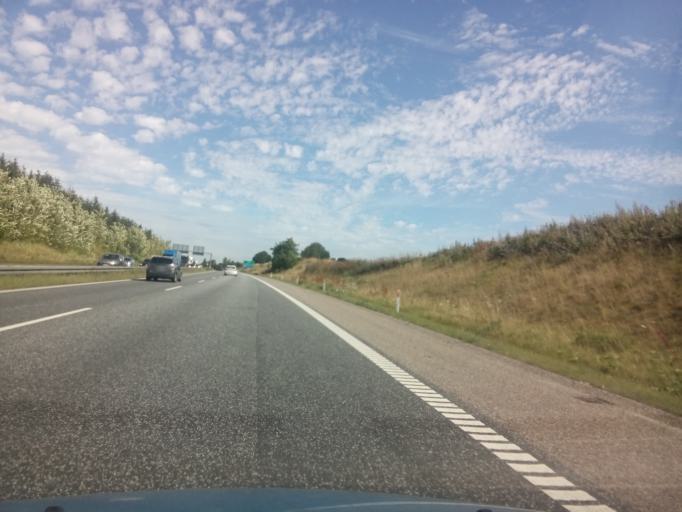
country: DK
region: Central Jutland
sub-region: Arhus Kommune
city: Trige
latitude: 56.2327
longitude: 10.1248
